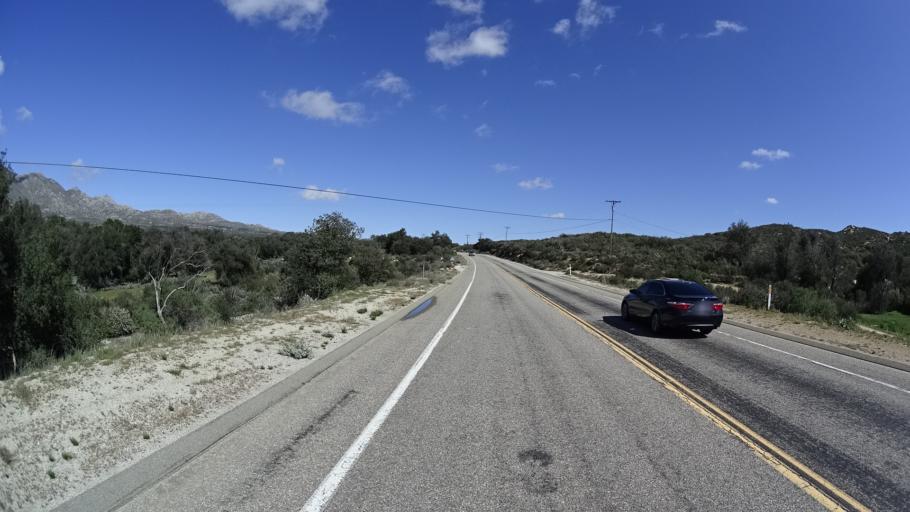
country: US
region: California
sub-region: San Diego County
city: Julian
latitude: 33.2105
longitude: -116.5440
